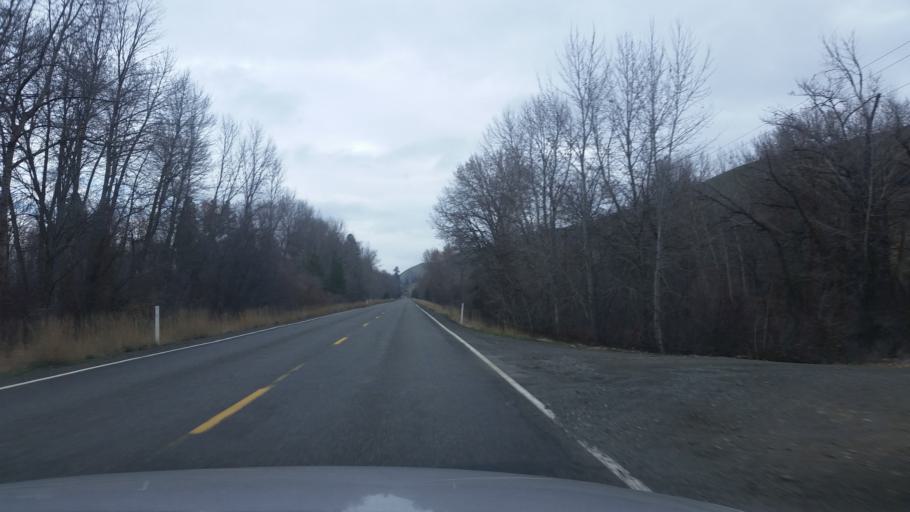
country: US
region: Washington
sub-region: Kittitas County
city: Ellensburg
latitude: 47.0619
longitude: -120.6484
